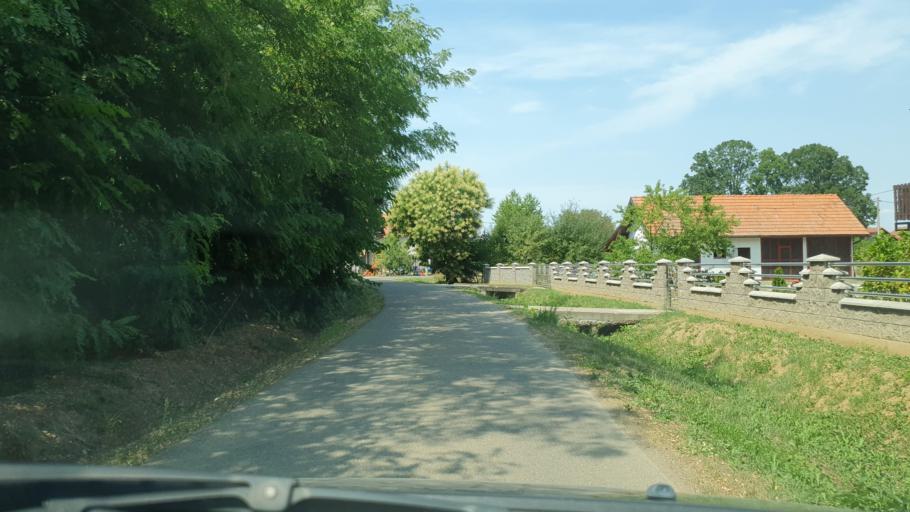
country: BA
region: Republika Srpska
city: Bijeljina
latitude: 44.7241
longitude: 19.2017
